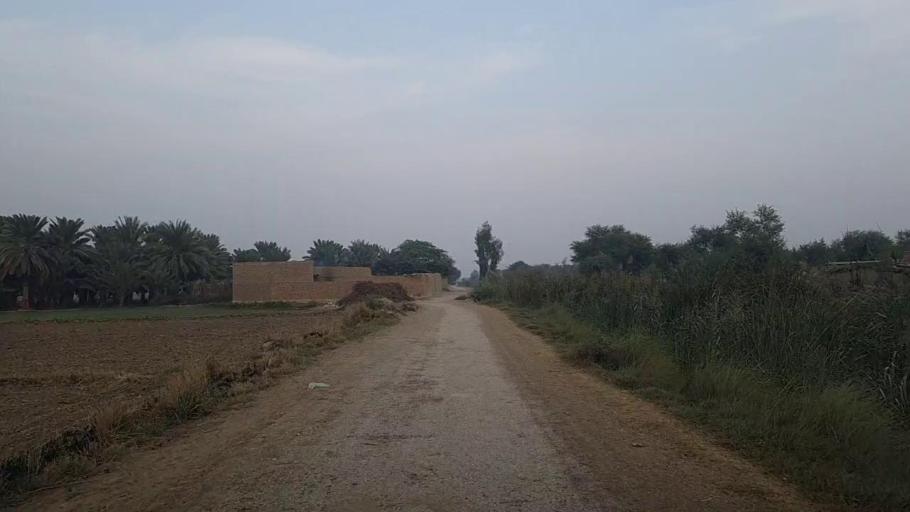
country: PK
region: Sindh
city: Kot Diji
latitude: 27.3573
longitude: 68.6672
